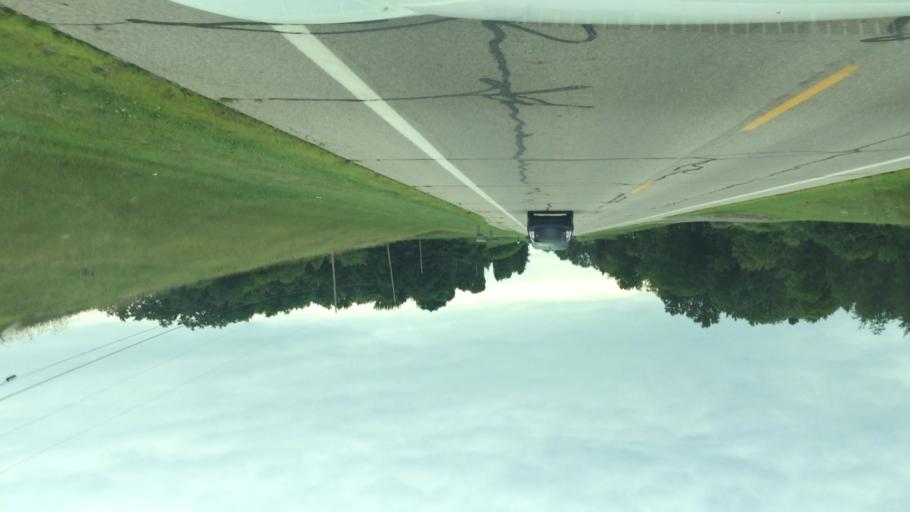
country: US
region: Ohio
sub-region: Champaign County
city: Mechanicsburg
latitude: 40.0784
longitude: -83.5911
